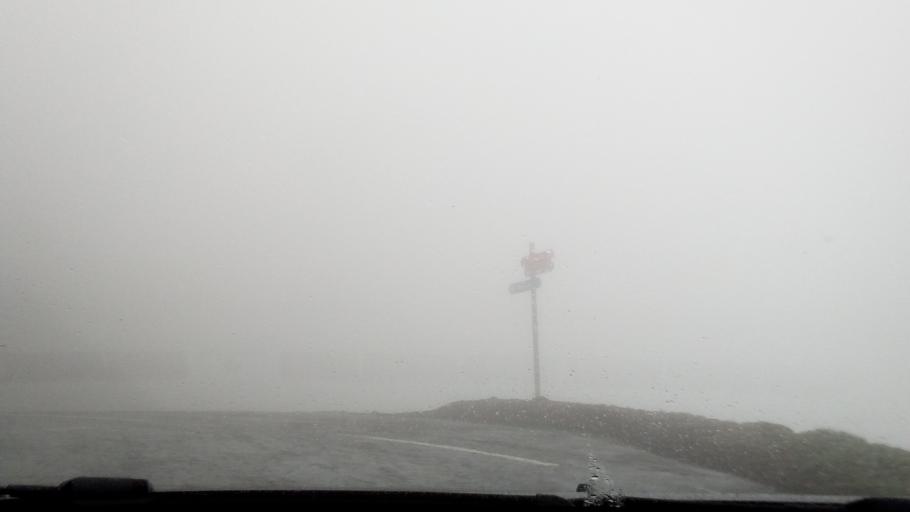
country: FR
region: Midi-Pyrenees
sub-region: Departement des Hautes-Pyrenees
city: Campan
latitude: 42.9052
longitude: 0.1465
